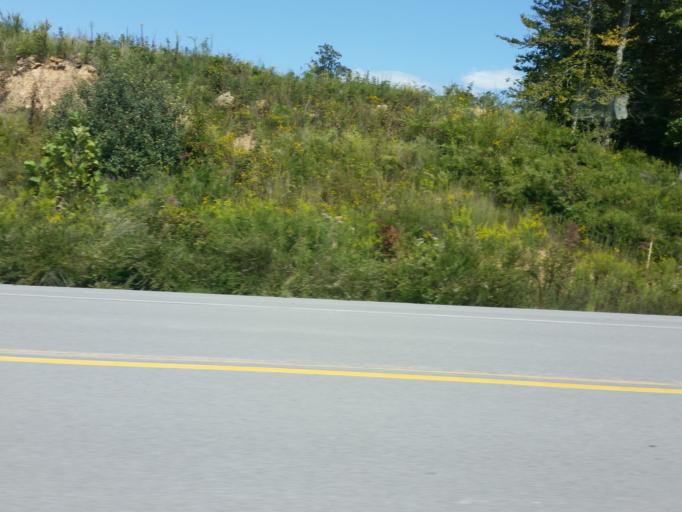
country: US
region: Kentucky
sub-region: Bell County
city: Pineville
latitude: 36.7457
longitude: -83.5917
